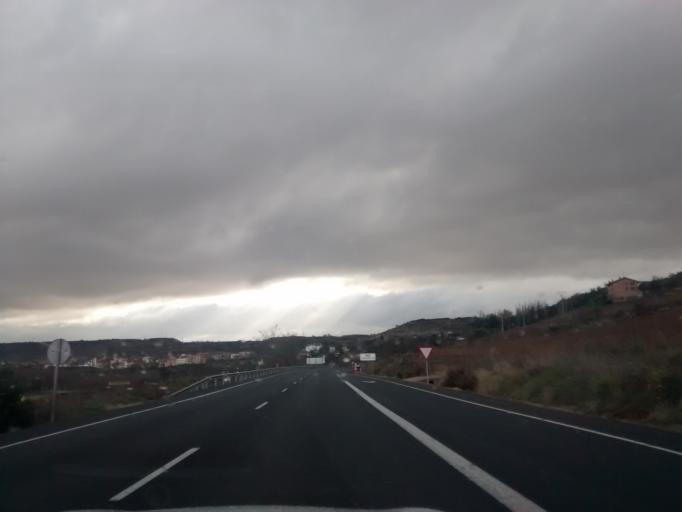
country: ES
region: La Rioja
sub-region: Provincia de La Rioja
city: Cenicero
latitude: 42.4883
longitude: -2.6601
